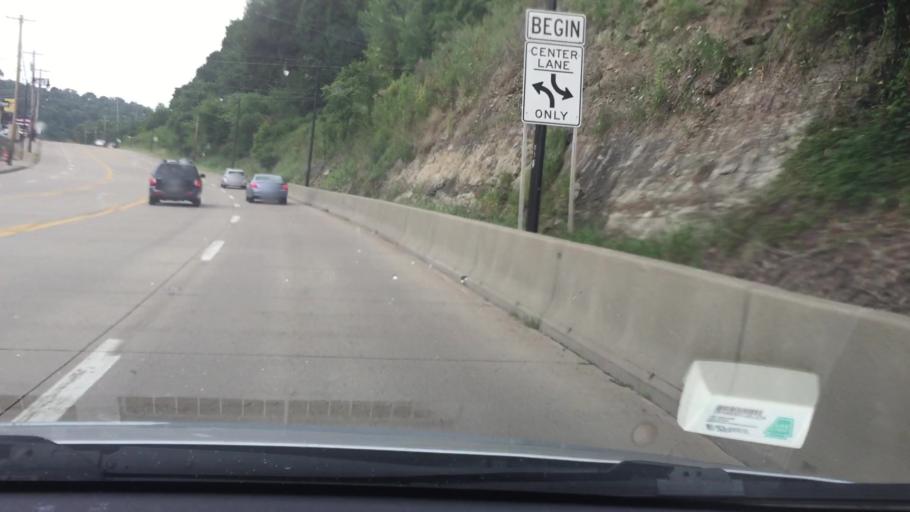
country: US
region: Pennsylvania
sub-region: Allegheny County
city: Etna
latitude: 40.5054
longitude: -79.9463
